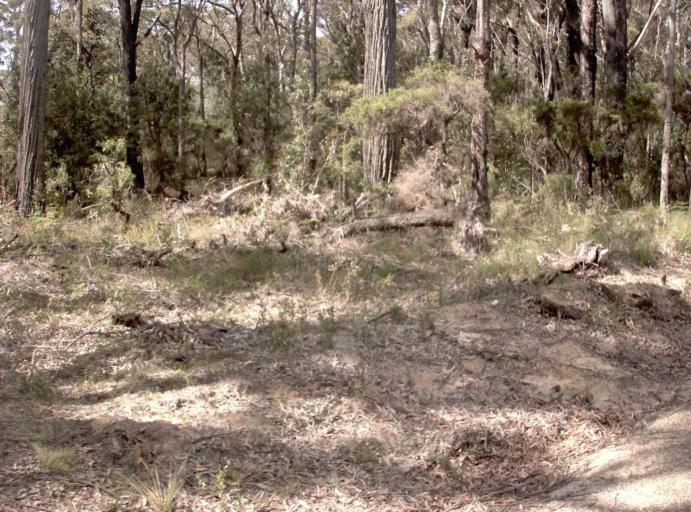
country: AU
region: New South Wales
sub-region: Bega Valley
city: Eden
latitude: -37.5446
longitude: 149.7041
